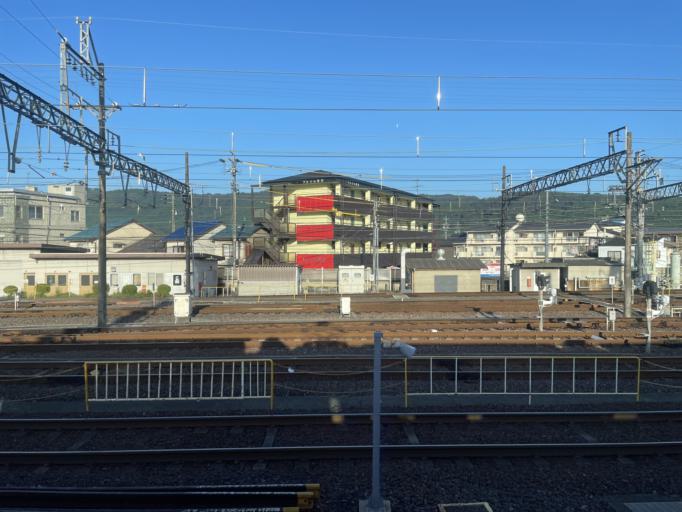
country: JP
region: Mie
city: Nabari
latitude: 34.6234
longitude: 136.0961
